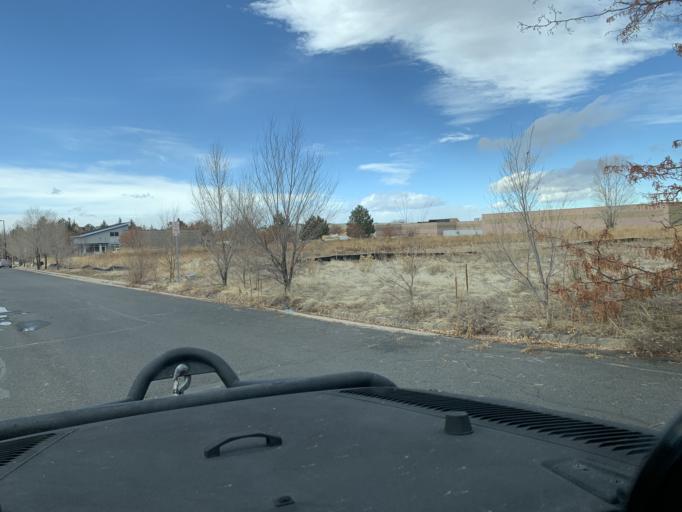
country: US
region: Colorado
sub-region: Adams County
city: Aurora
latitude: 39.7227
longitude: -104.8039
